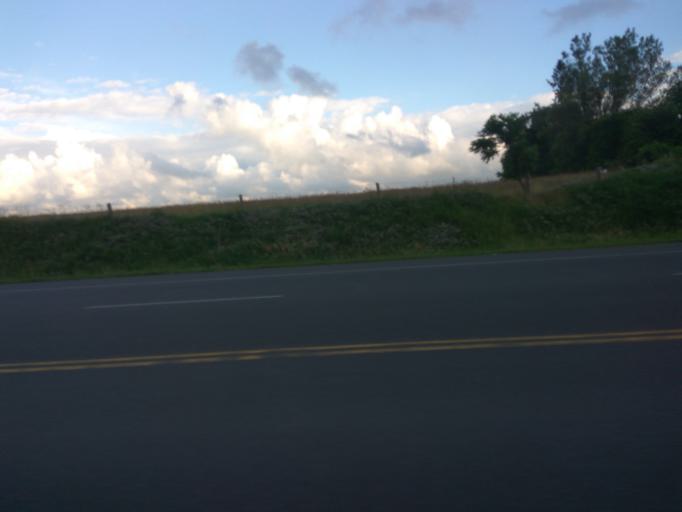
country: CA
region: Ontario
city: Stratford
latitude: 43.3702
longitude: -80.9163
